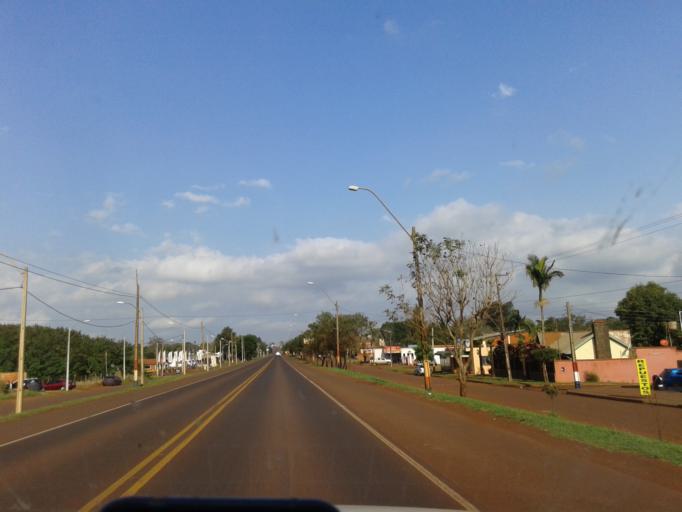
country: PY
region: Itapua
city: Arquitecto Tomas Romero Pereira
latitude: -26.5162
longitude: -55.2714
